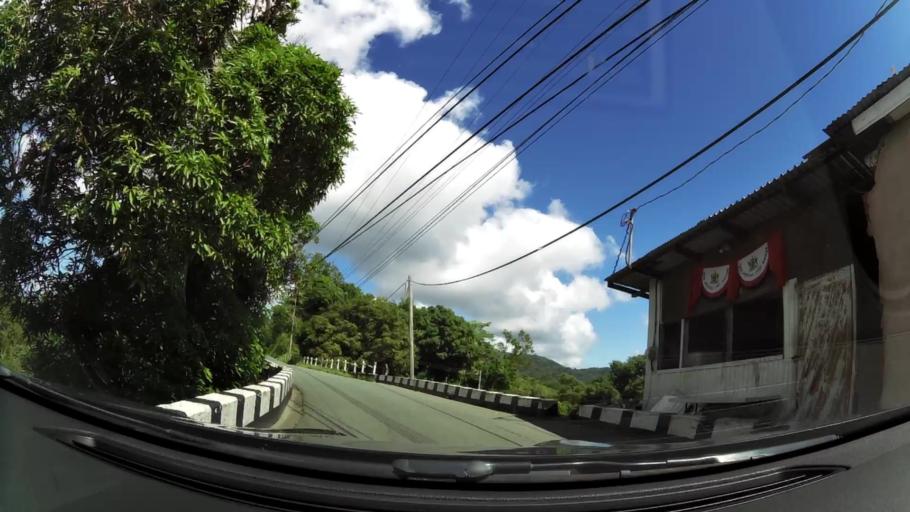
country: TT
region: Tobago
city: Scarborough
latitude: 11.2500
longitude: -60.7168
